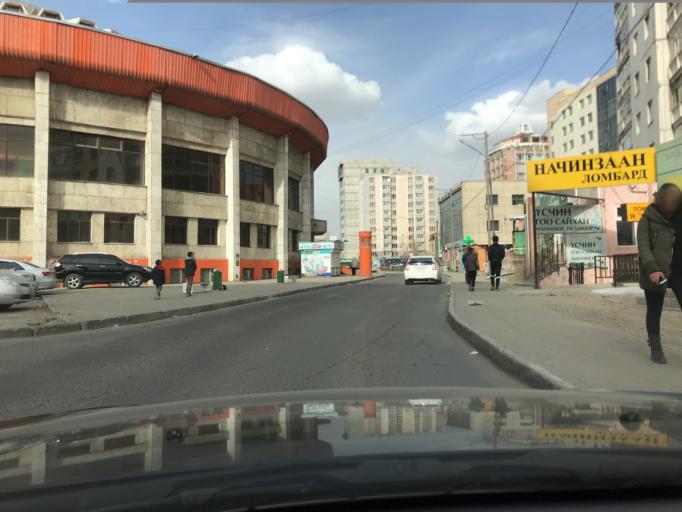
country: MN
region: Ulaanbaatar
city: Ulaanbaatar
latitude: 47.9173
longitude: 106.9357
